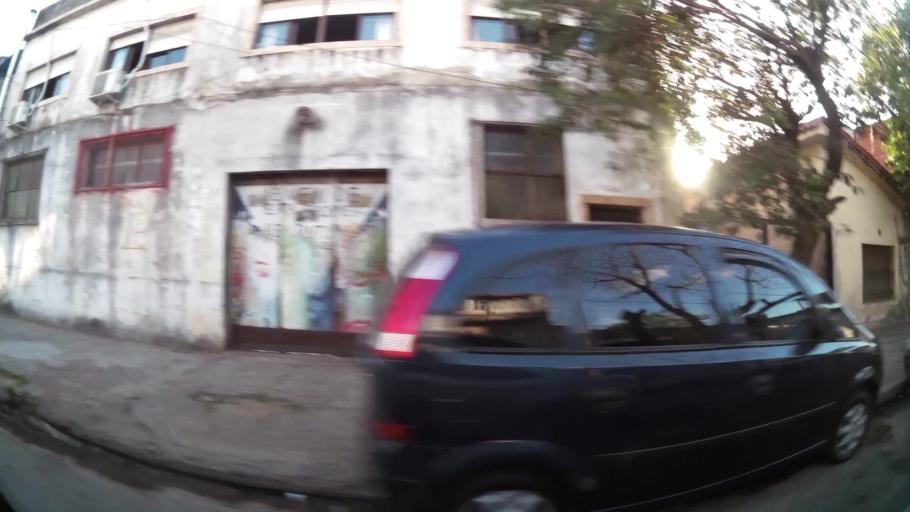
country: AR
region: Buenos Aires F.D.
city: Villa Lugano
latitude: -34.6910
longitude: -58.4839
